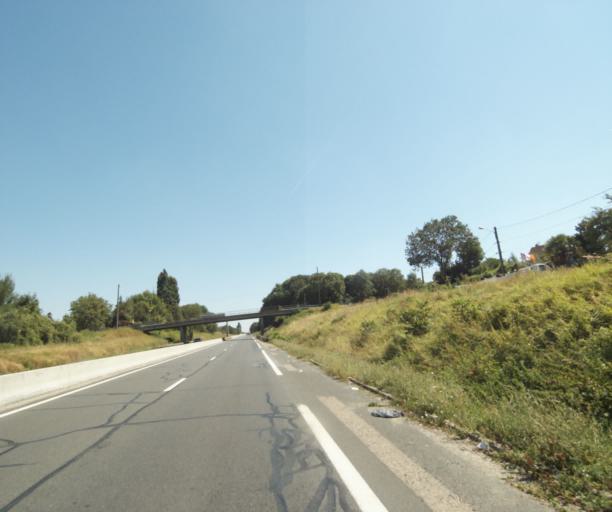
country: FR
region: Ile-de-France
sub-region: Departement de Seine-et-Marne
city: Gouvernes
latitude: 48.8664
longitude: 2.6894
